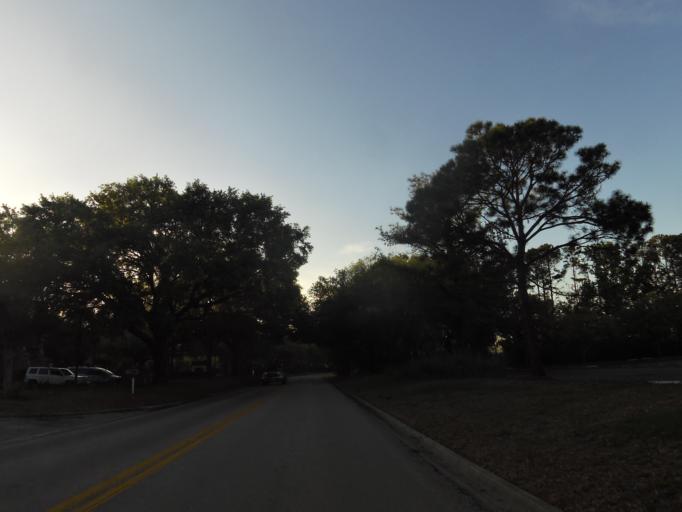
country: US
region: Florida
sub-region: Duval County
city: Jacksonville
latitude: 30.2553
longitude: -81.5900
